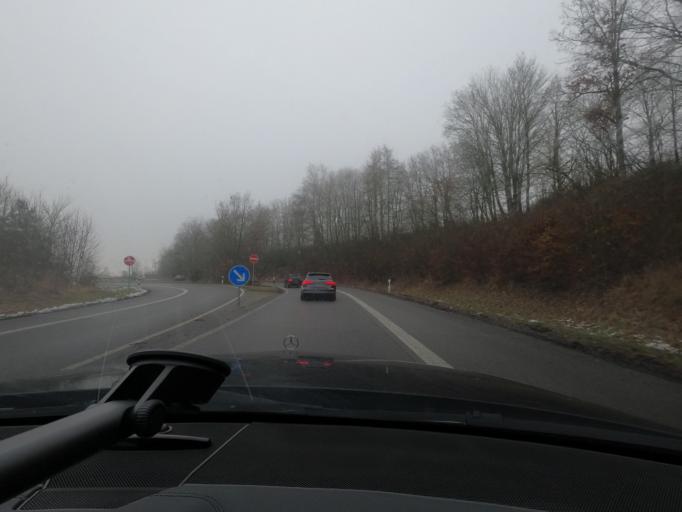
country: DE
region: Hesse
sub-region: Regierungsbezirk Kassel
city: Martinhagen
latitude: 51.3196
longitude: 9.2832
